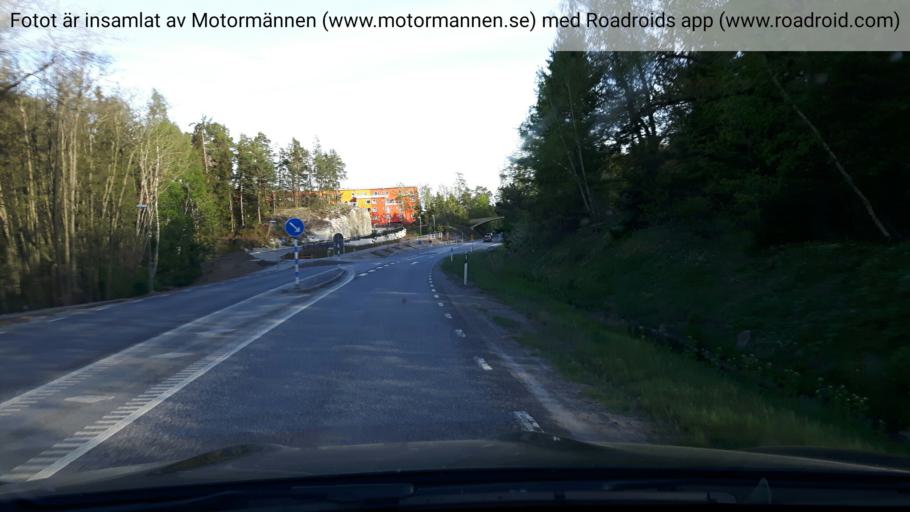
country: SE
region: Stockholm
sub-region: Vaxholms Kommun
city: Resaro
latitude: 59.4144
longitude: 18.3156
